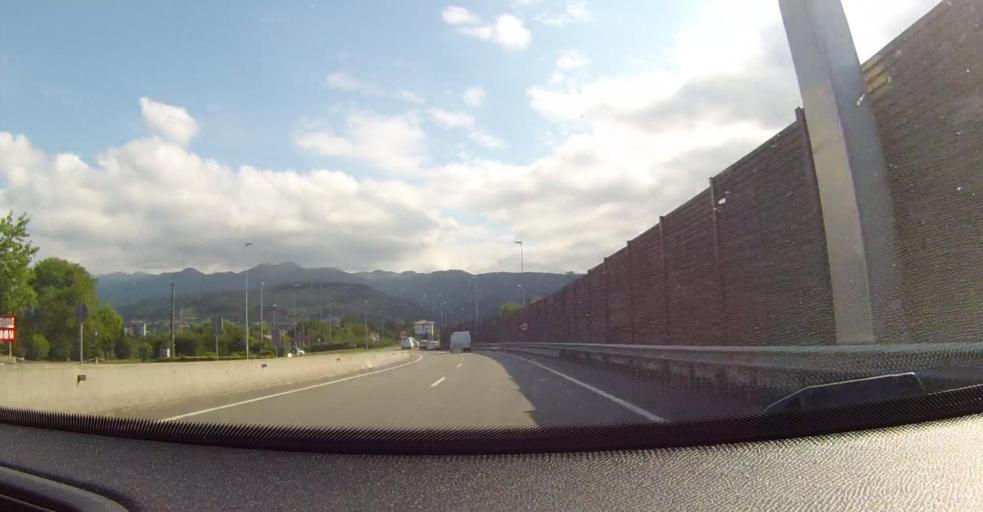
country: ES
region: Basque Country
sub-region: Bizkaia
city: Amorebieta
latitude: 43.2274
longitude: -2.7306
